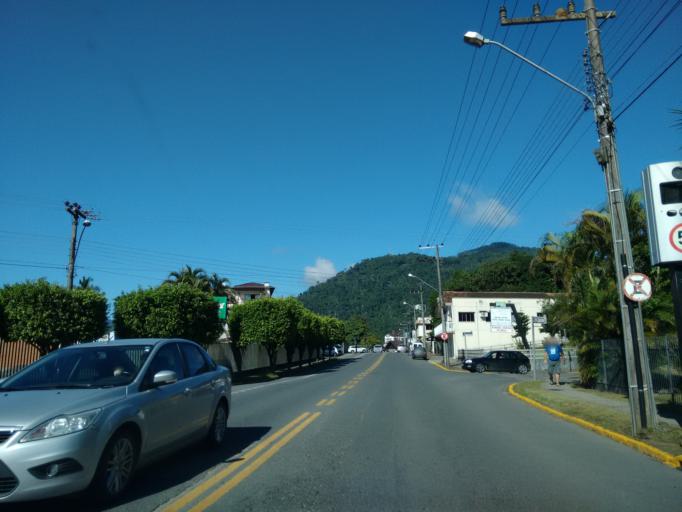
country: BR
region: Santa Catarina
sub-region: Pomerode
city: Pomerode
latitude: -26.7278
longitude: -49.1743
